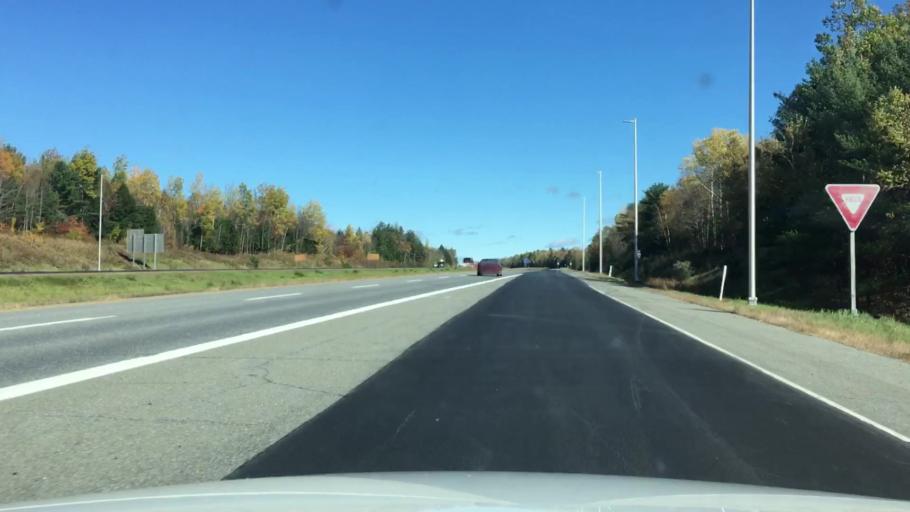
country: US
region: Maine
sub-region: Penobscot County
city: Medway
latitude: 45.6093
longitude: -68.5187
